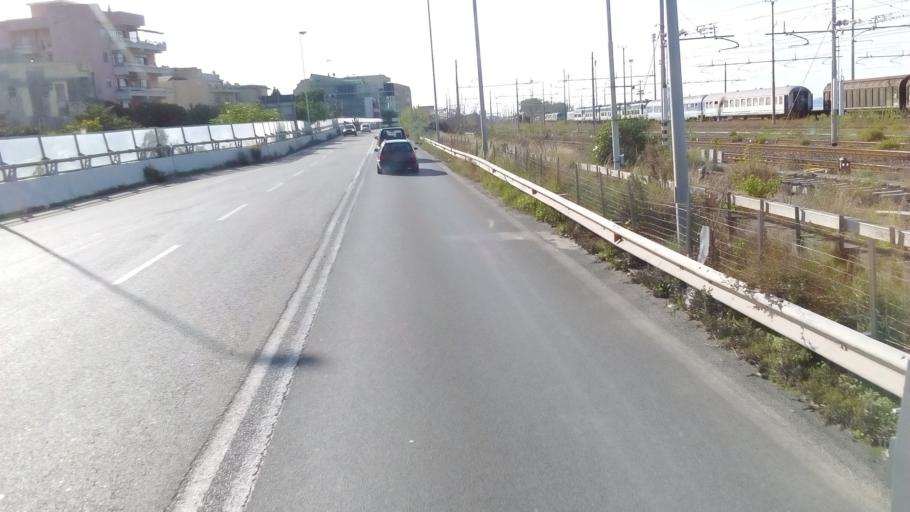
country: IT
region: Calabria
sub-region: Provincia di Reggio Calabria
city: Campo Calabro
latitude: 38.2113
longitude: 15.6354
